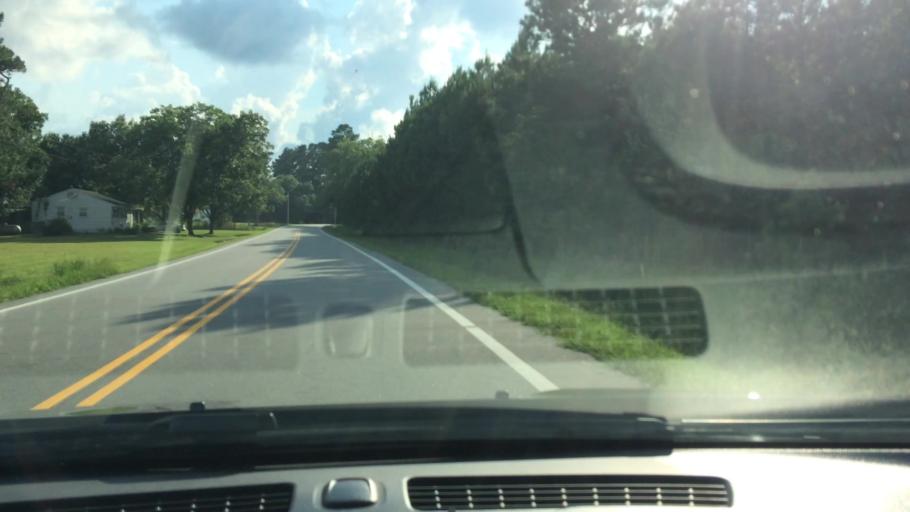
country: US
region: North Carolina
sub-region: Craven County
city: Vanceboro
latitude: 35.4292
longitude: -77.1935
